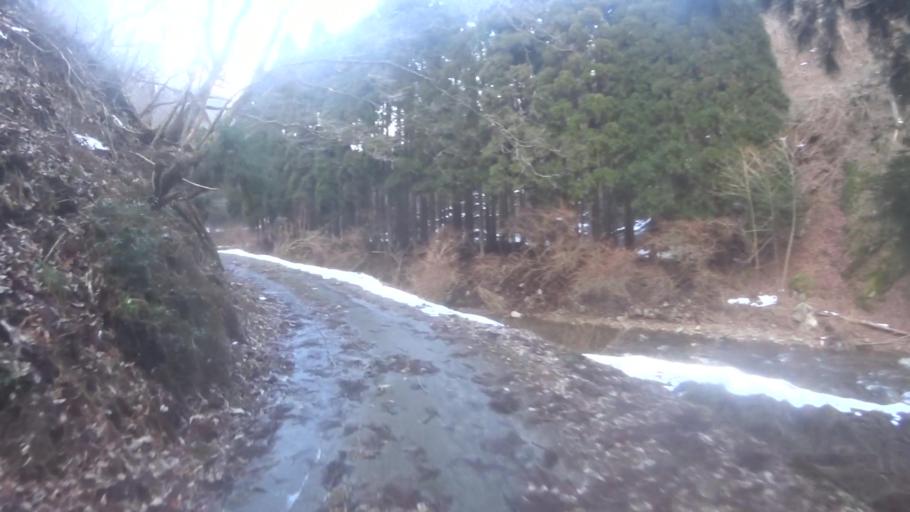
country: JP
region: Kyoto
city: Maizuru
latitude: 35.4016
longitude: 135.5020
